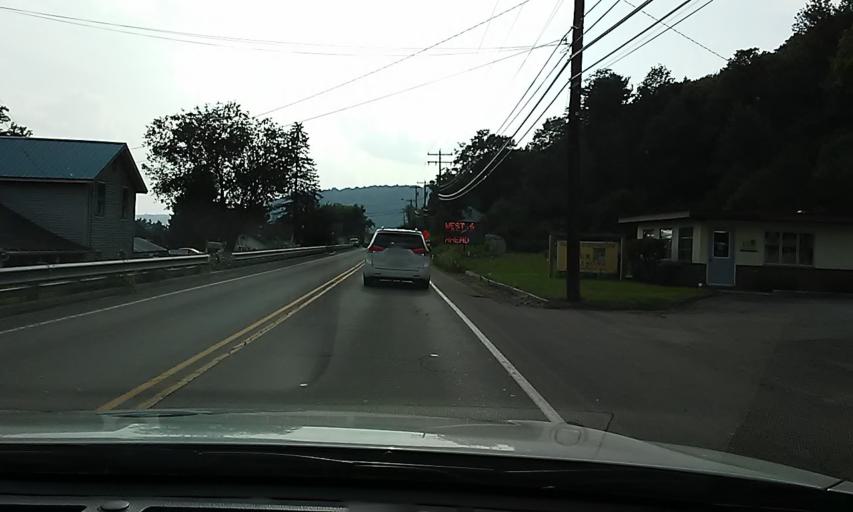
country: US
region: Pennsylvania
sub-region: Potter County
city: Coudersport
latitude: 41.7747
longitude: -78.0081
